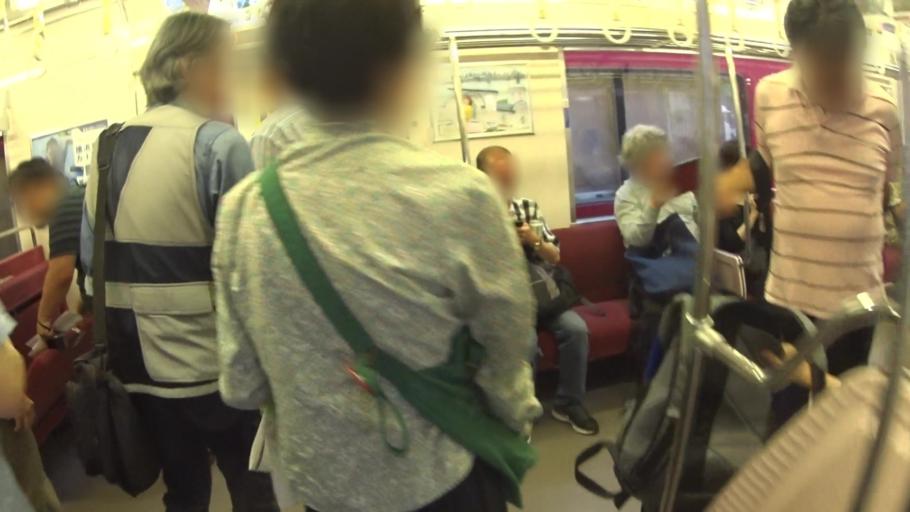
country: JP
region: Kanagawa
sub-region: Kawasaki-shi
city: Kawasaki
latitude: 35.5157
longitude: 139.6852
